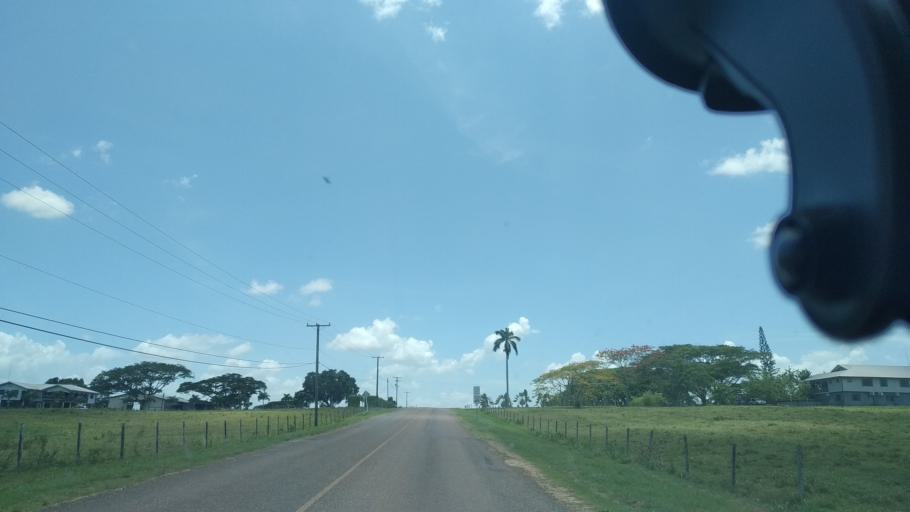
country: BZ
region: Cayo
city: San Ignacio
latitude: 17.2566
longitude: -88.9878
